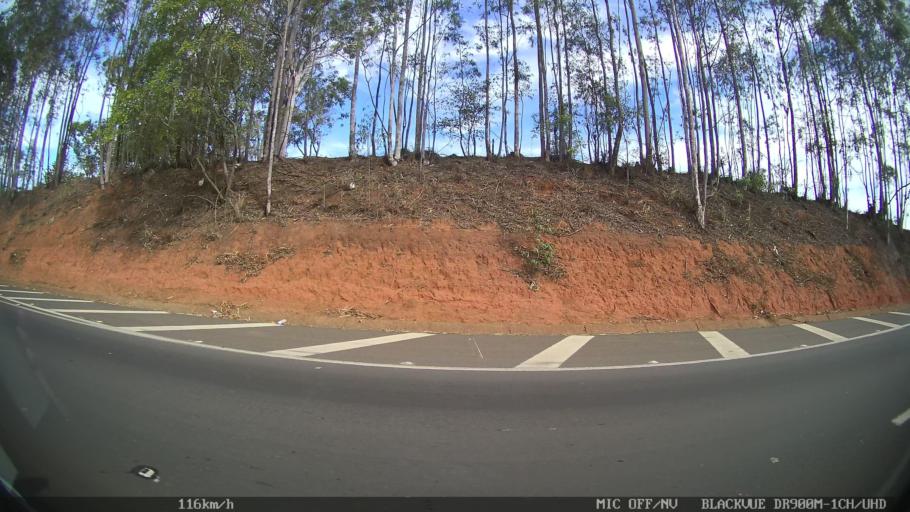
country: BR
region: Sao Paulo
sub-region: Taquaritinga
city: Taquaritinga
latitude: -21.5384
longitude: -48.5078
